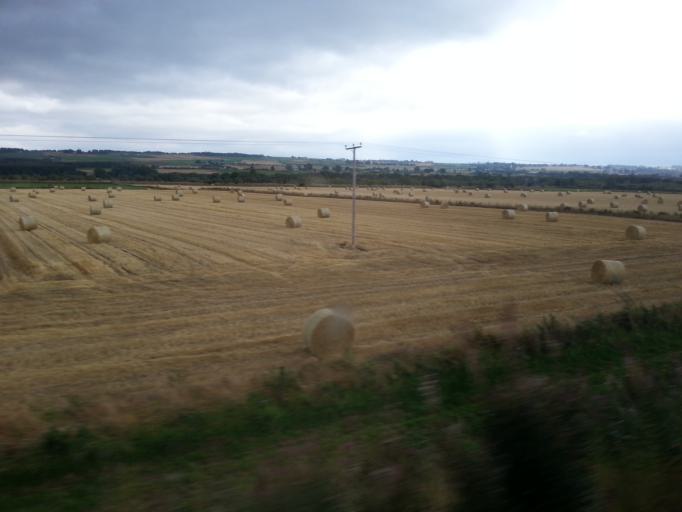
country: GB
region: Scotland
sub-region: Highland
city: Dingwall
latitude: 57.5825
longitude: -4.4302
